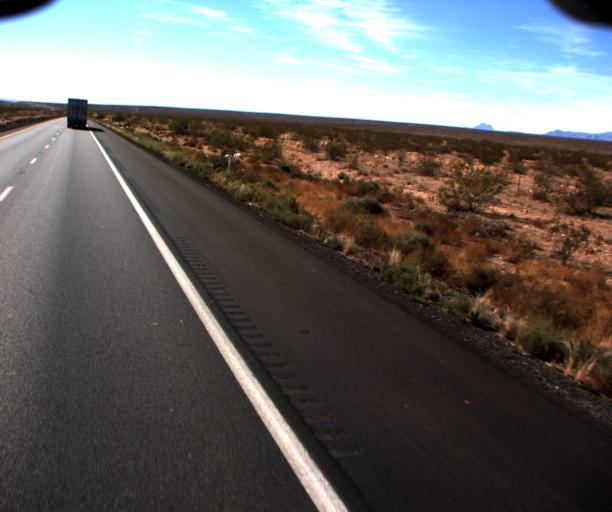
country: US
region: Arizona
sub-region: Mohave County
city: Beaver Dam
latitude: 36.8733
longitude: -113.9590
